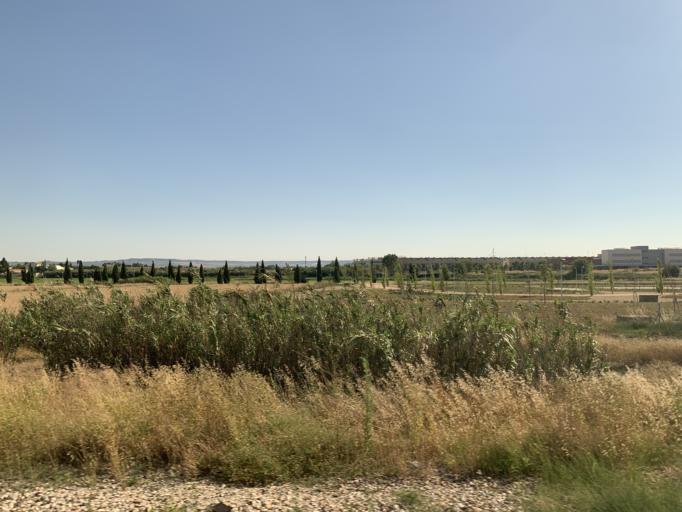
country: ES
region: Aragon
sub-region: Provincia de Zaragoza
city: Utebo
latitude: 41.7054
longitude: -0.9894
